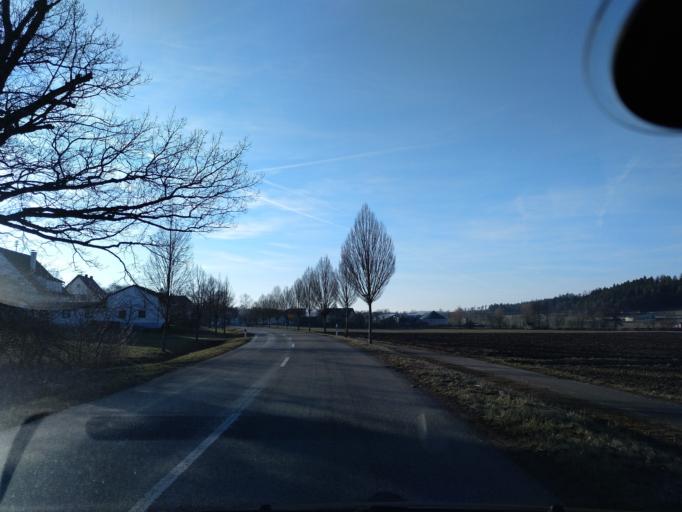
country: DE
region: Baden-Wuerttemberg
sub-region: Regierungsbezirk Stuttgart
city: Crailsheim
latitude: 49.0899
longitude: 10.0271
